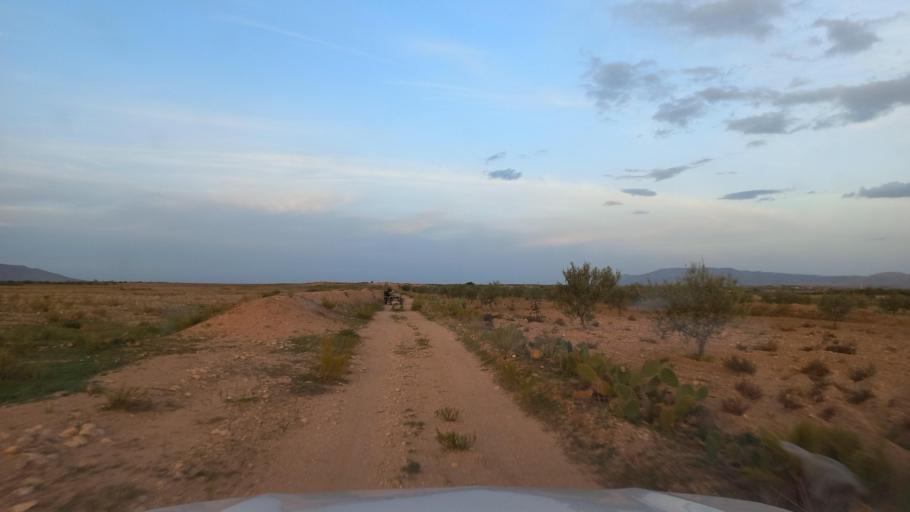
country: TN
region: Al Qasrayn
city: Sbiba
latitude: 35.3502
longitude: 9.0244
